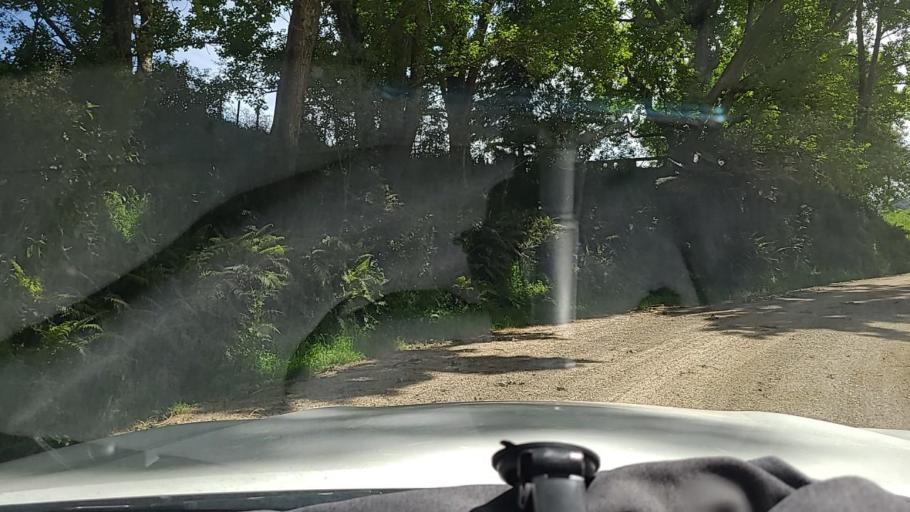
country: NZ
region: Hawke's Bay
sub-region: Wairoa District
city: Wairoa
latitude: -38.5418
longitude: 177.4051
